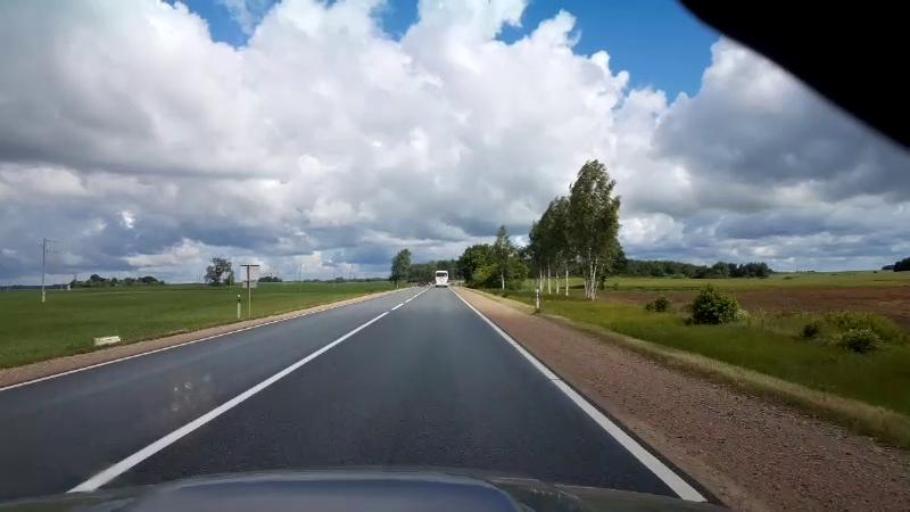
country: LV
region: Lecava
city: Iecava
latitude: 56.5083
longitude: 24.1729
